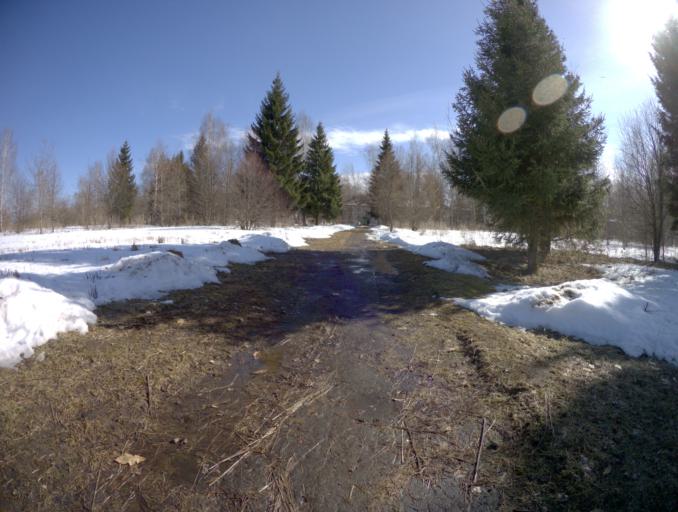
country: RU
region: Vladimir
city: Suzdal'
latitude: 56.4428
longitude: 40.4600
